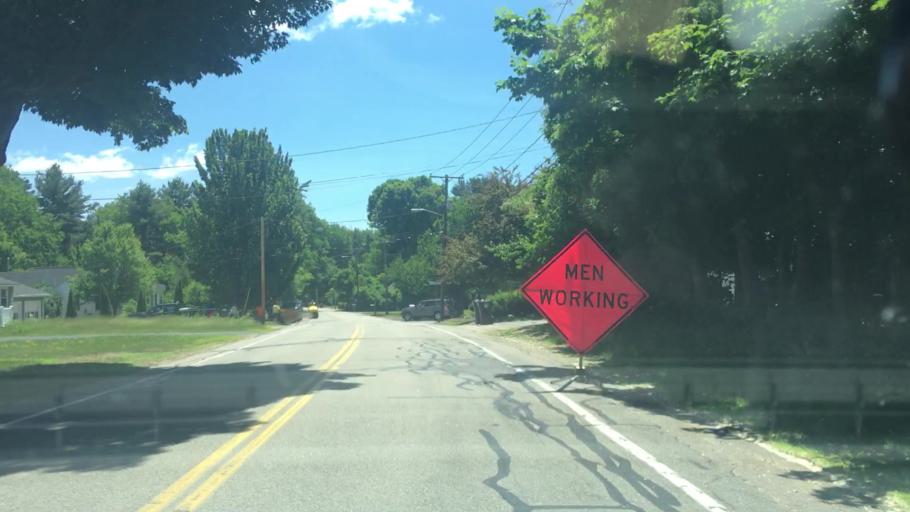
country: US
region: Maine
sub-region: York County
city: Kennebunk
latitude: 43.3687
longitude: -70.5251
